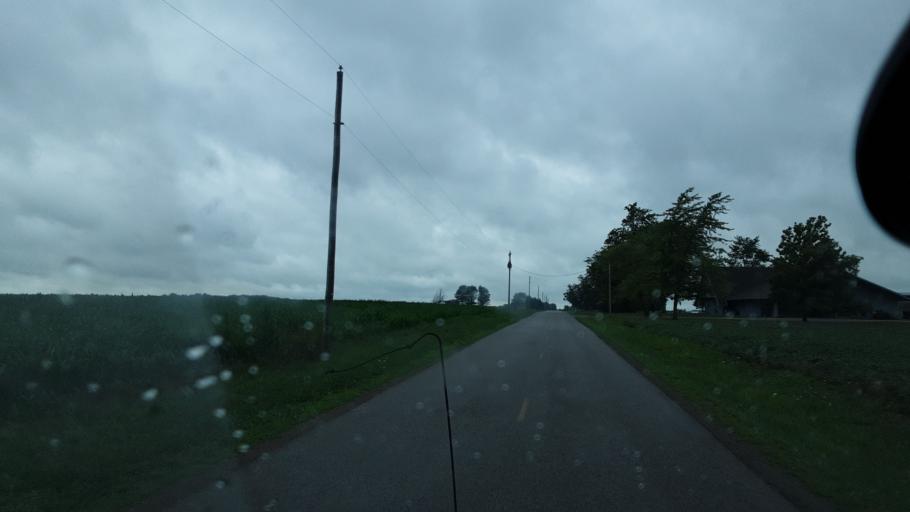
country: US
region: Ohio
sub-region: Van Wert County
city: Van Wert
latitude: 40.8004
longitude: -84.6535
